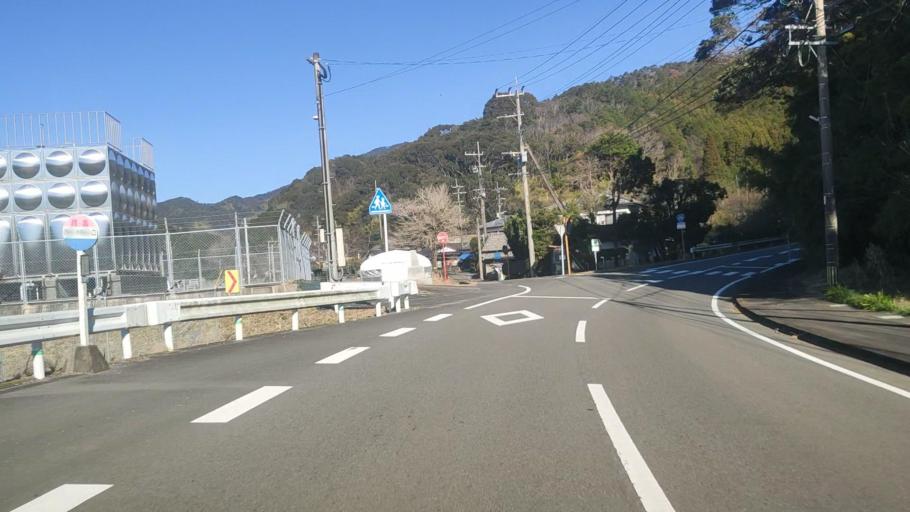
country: JP
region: Miyazaki
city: Nobeoka
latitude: 32.6675
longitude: 131.7662
